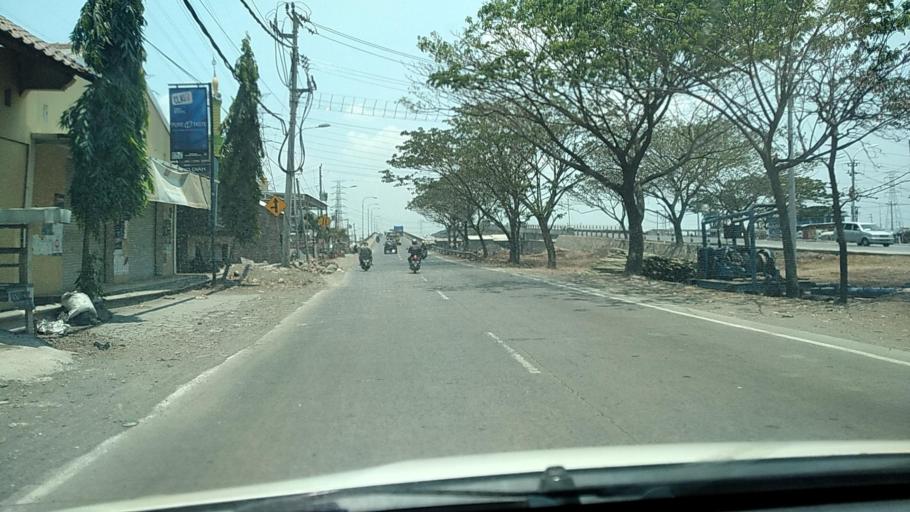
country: ID
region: Central Java
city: Semarang
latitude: -6.9511
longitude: 110.4381
